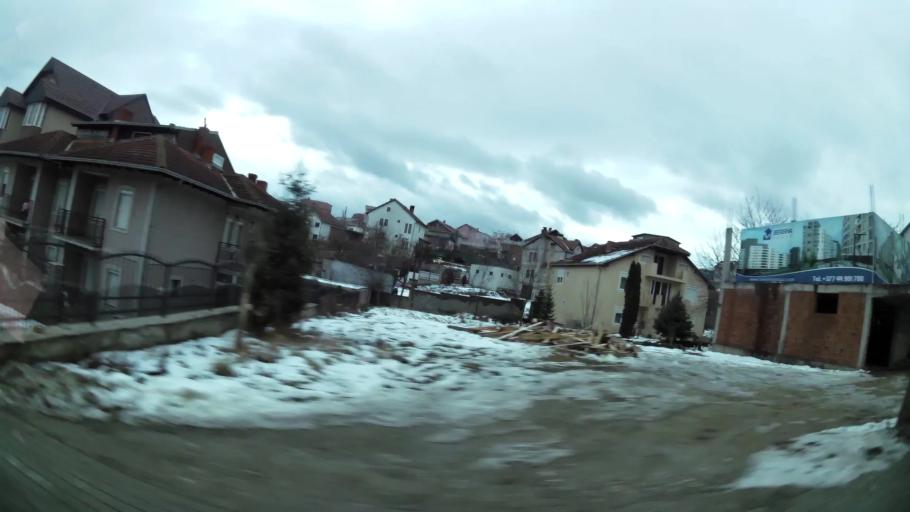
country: XK
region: Pristina
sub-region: Komuna e Prishtines
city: Pristina
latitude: 42.6393
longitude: 21.1636
